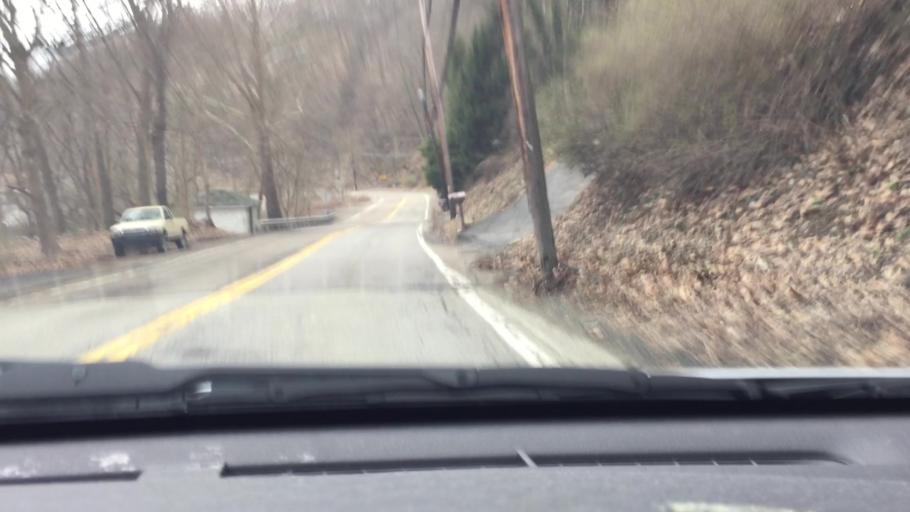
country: US
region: Pennsylvania
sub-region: Allegheny County
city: Allison Park
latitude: 40.5619
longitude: -79.9656
